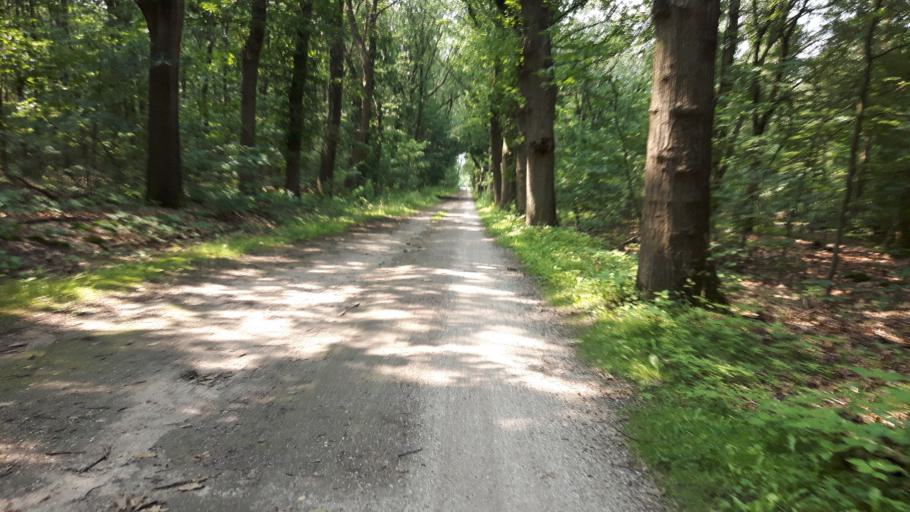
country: NL
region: Utrecht
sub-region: Gemeente Zeist
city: Zeist
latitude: 52.1027
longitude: 5.2751
